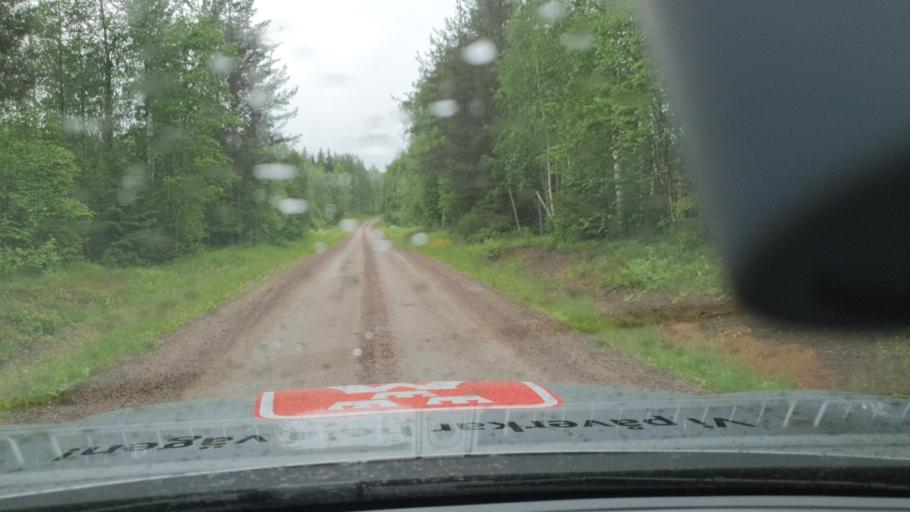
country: SE
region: Norrbotten
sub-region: Overkalix Kommun
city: OEverkalix
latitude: 66.5042
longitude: 22.7544
